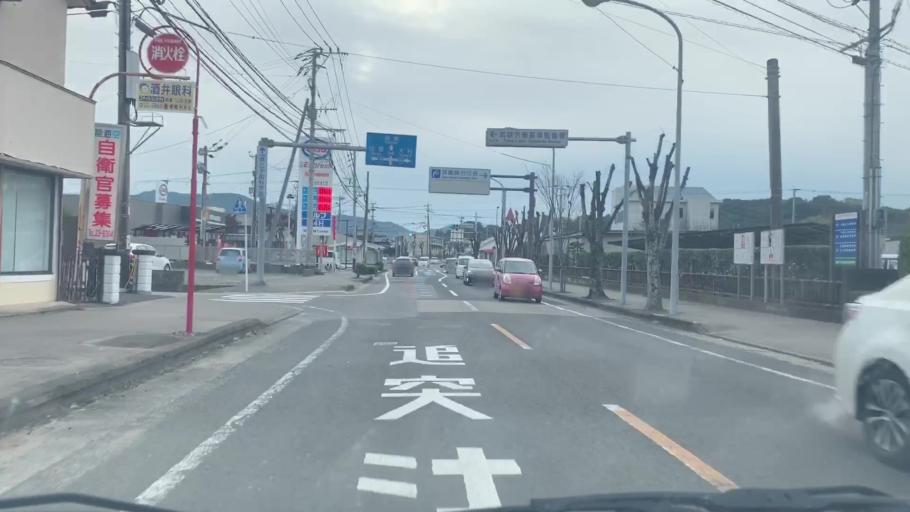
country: JP
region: Saga Prefecture
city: Takeocho-takeo
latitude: 33.1957
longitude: 130.0285
